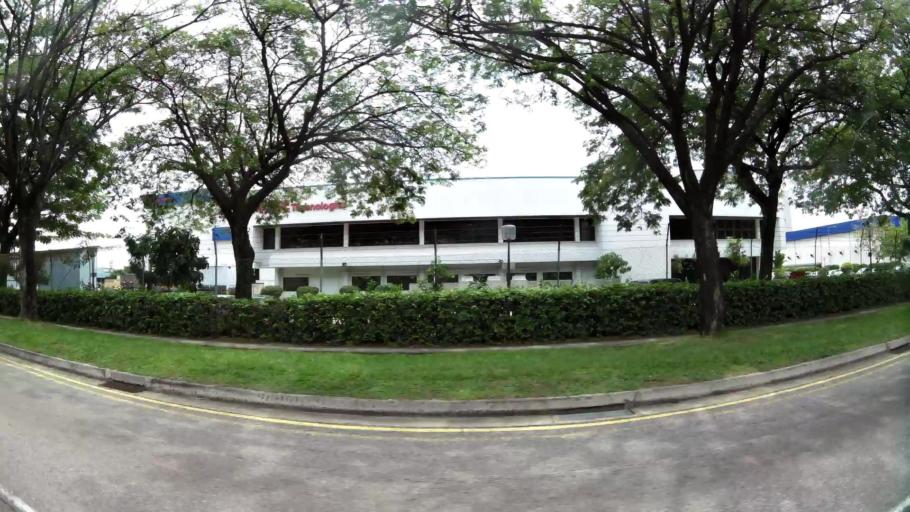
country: MY
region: Johor
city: Johor Bahru
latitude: 1.3221
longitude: 103.6730
